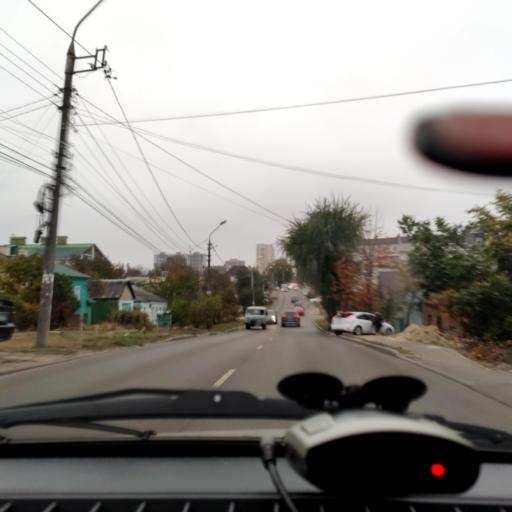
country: RU
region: Voronezj
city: Voronezh
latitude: 51.6929
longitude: 39.1902
